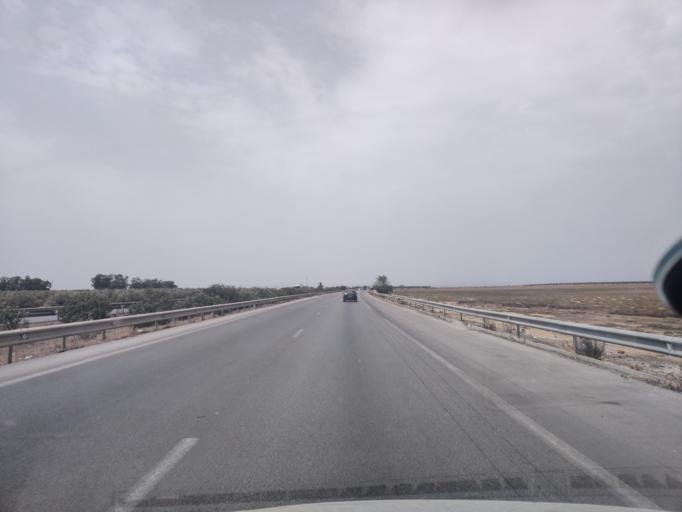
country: TN
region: Susah
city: Sidi Bou Ali
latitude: 35.9816
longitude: 10.4505
